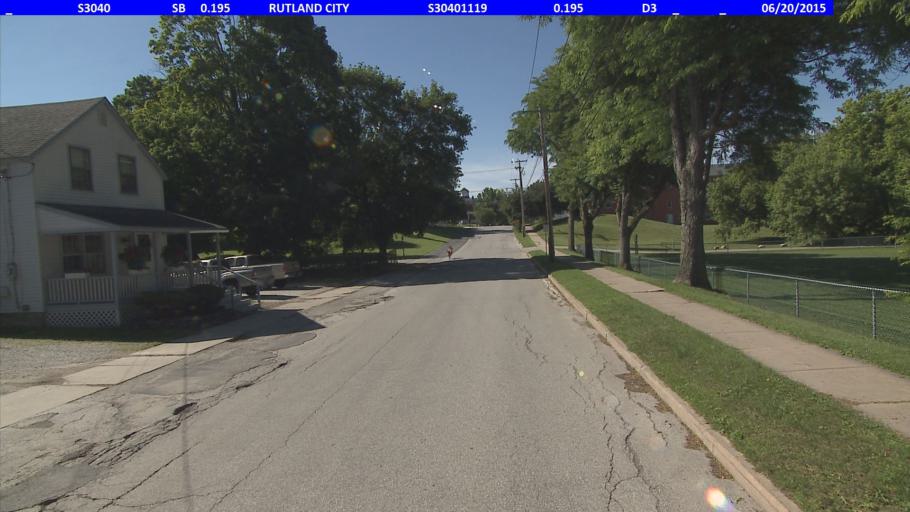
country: US
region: Vermont
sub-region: Rutland County
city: Rutland
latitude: 43.6040
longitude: -72.9866
